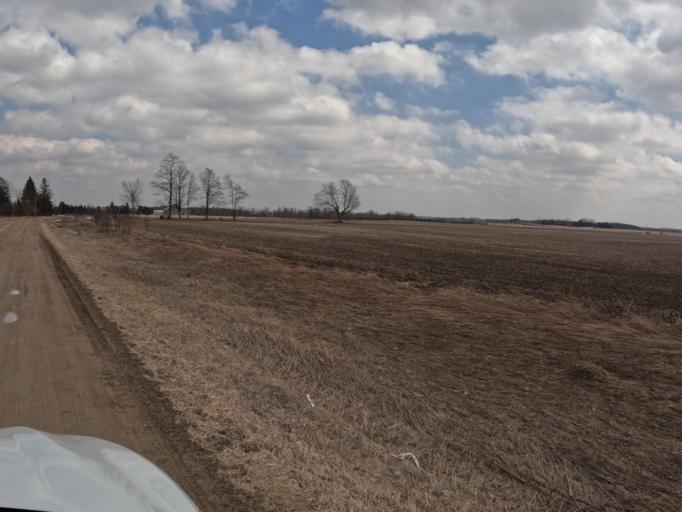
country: CA
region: Ontario
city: Shelburne
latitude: 44.0258
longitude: -80.2727
